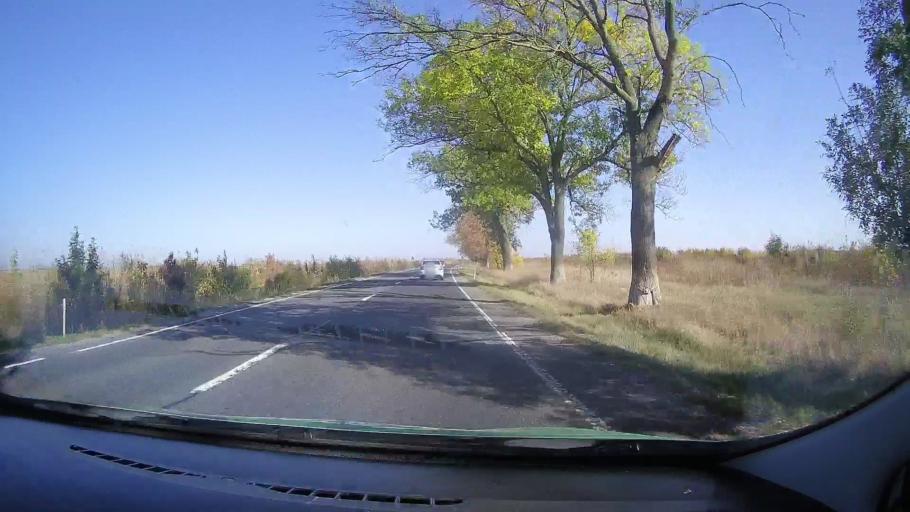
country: RO
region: Satu Mare
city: Moftinu Mare
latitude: 47.7137
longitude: 22.6474
